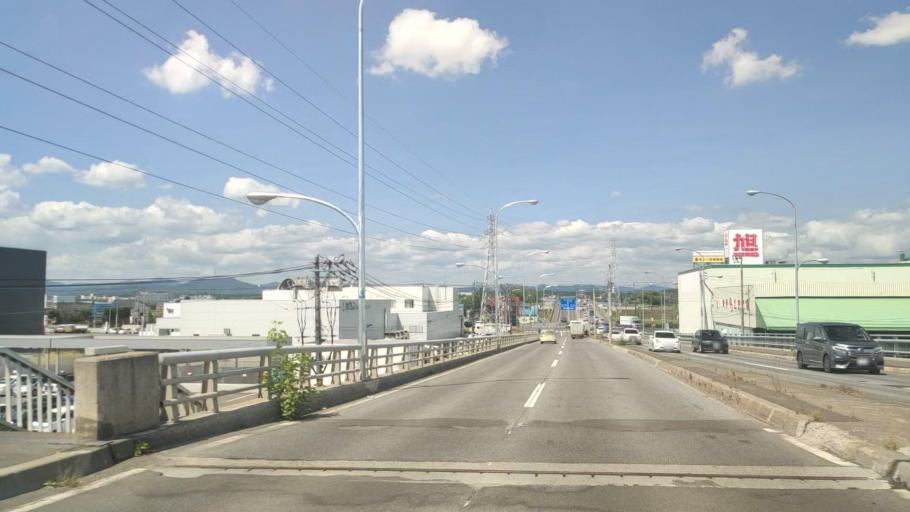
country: JP
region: Hokkaido
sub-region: Asahikawa-shi
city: Asahikawa
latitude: 43.7942
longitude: 142.4004
